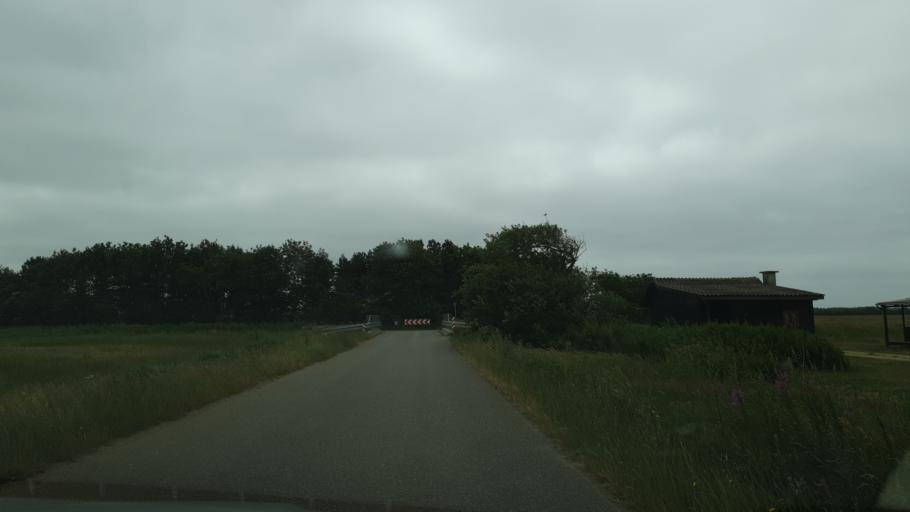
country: DK
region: Central Jutland
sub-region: Ringkobing-Skjern Kommune
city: Skjern
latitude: 55.9232
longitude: 8.4016
